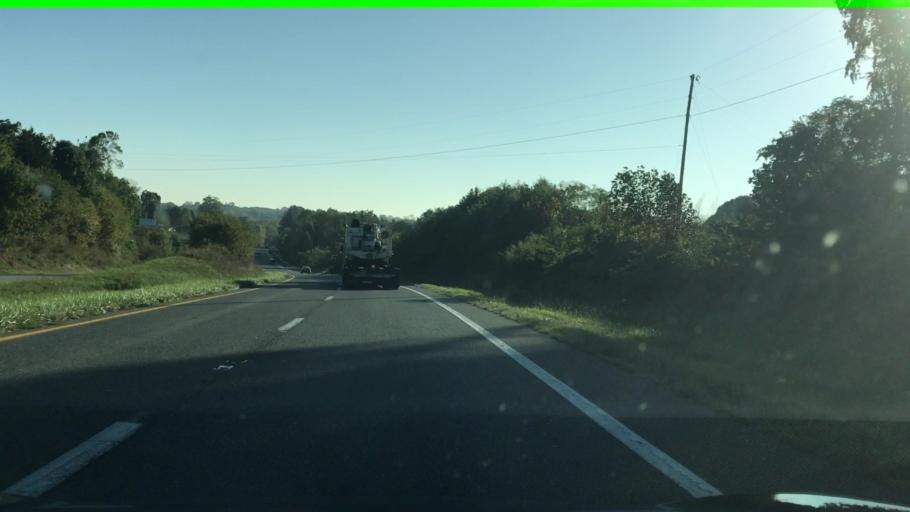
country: US
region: Virginia
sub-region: City of Bedford
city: Bedford
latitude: 37.3146
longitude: -79.4544
